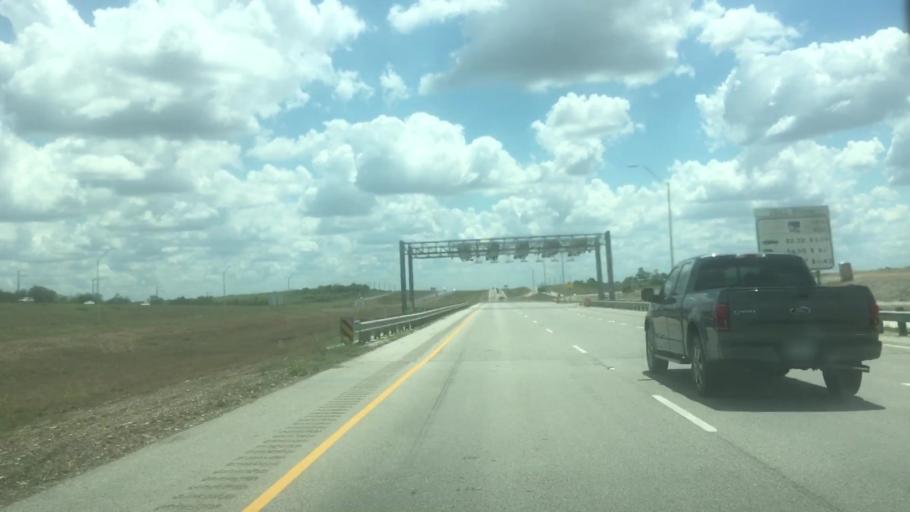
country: US
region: Texas
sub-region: Caldwell County
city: Lockhart
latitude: 29.9905
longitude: -97.6842
